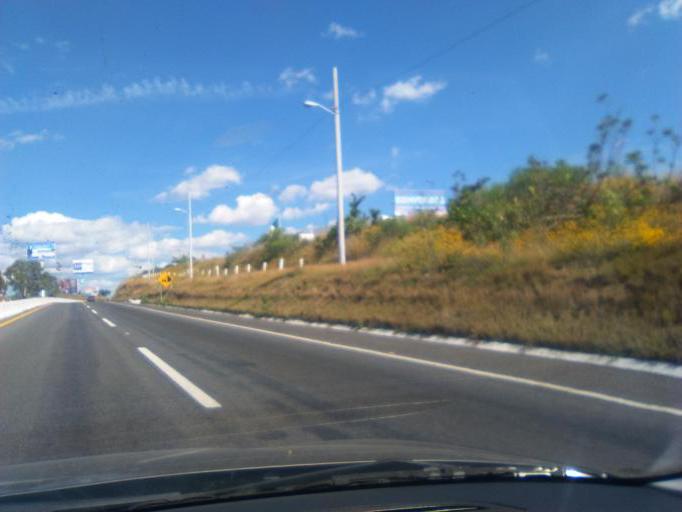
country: MX
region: Guanajuato
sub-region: Silao de la Victoria
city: Aguas Buenas
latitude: 20.9577
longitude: -101.3633
